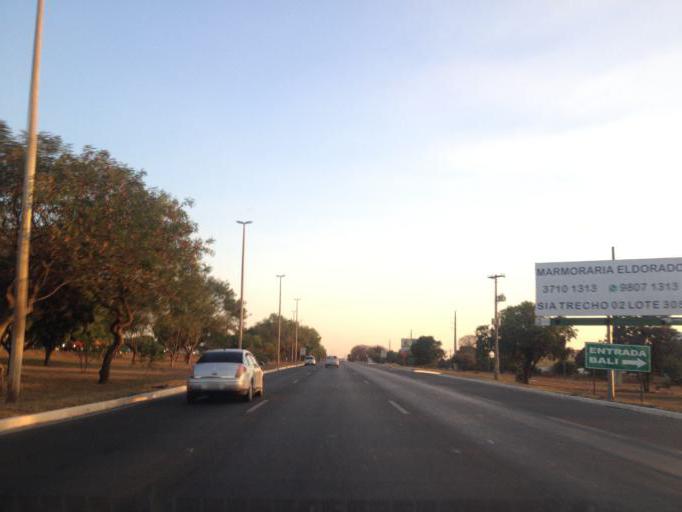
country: BR
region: Federal District
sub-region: Brasilia
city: Brasilia
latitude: -15.7642
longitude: -47.9321
